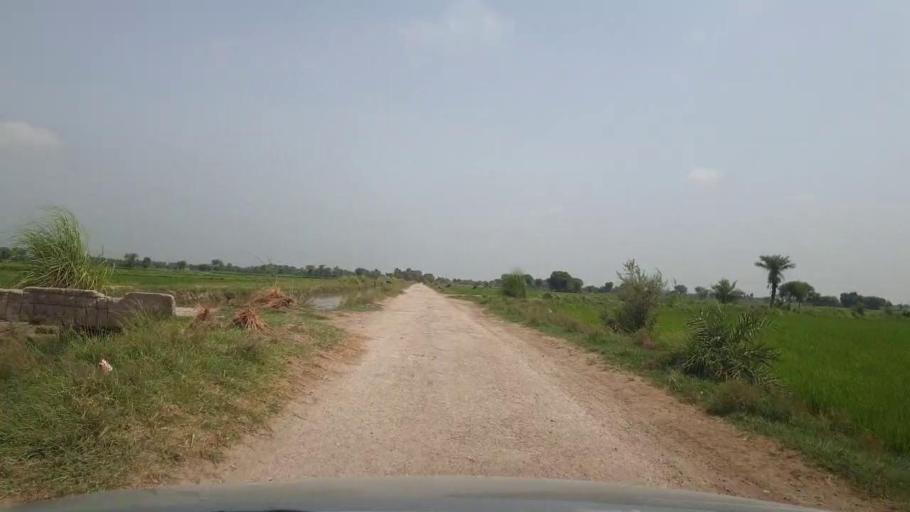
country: PK
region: Sindh
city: Ratodero
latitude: 27.9288
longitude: 68.3612
